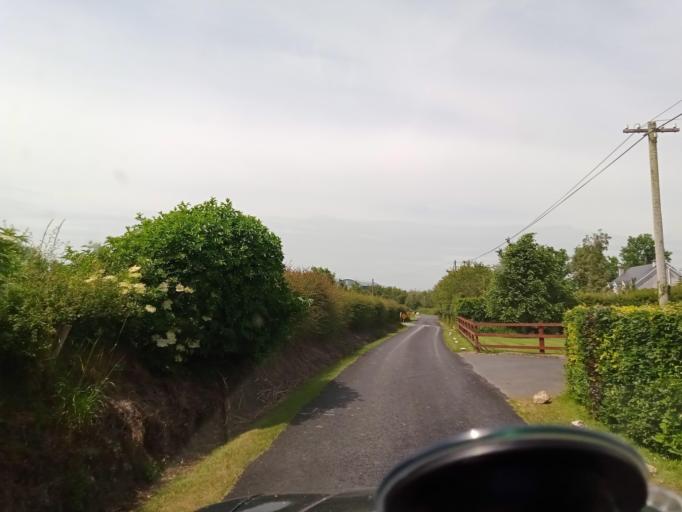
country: IE
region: Leinster
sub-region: Kilkenny
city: Thomastown
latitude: 52.5572
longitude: -7.1116
